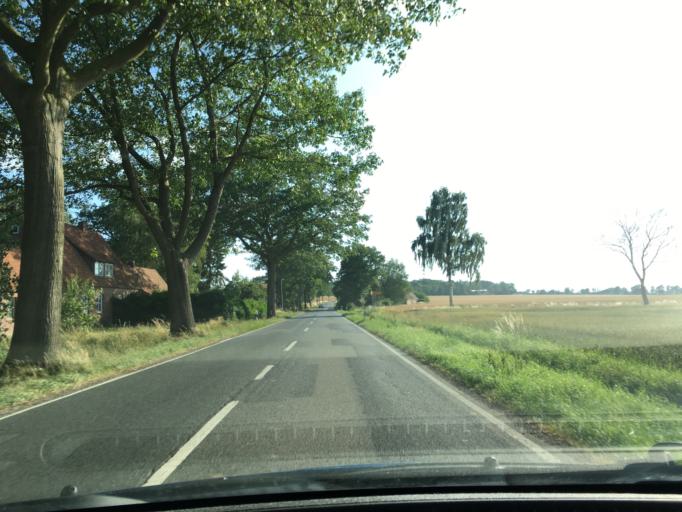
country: DE
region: Lower Saxony
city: Altenmedingen
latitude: 53.1375
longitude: 10.6353
